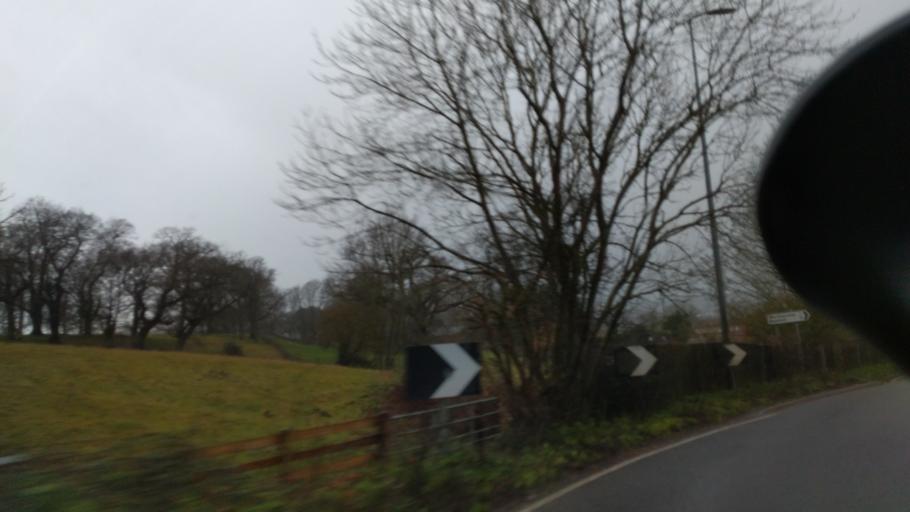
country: GB
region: England
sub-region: West Sussex
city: Arundel
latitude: 50.8471
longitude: -0.5440
